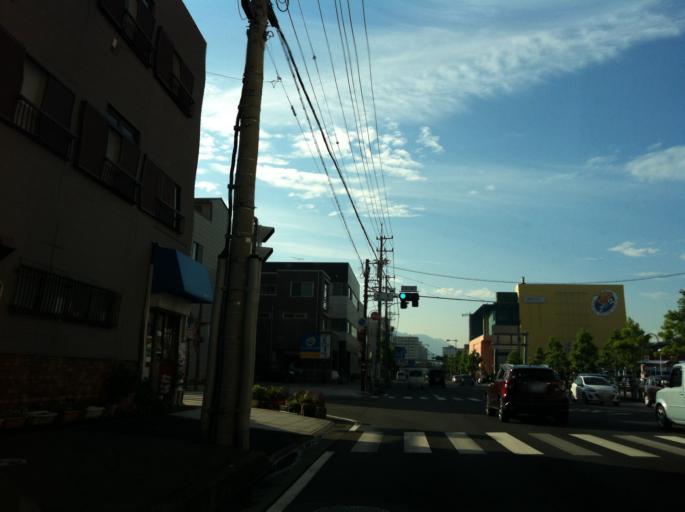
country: JP
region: Shizuoka
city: Shizuoka-shi
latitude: 35.0043
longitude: 138.4948
